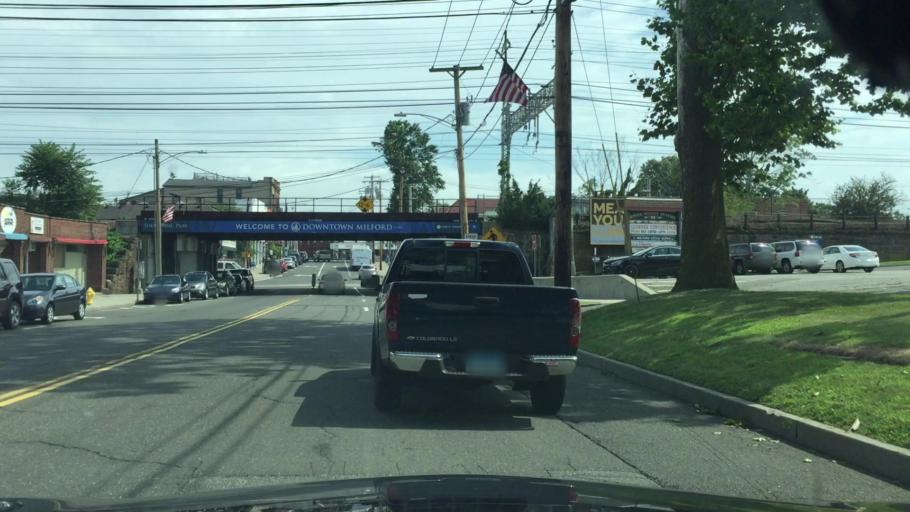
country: US
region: Connecticut
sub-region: New Haven County
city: Milford
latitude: 41.2239
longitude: -73.0575
